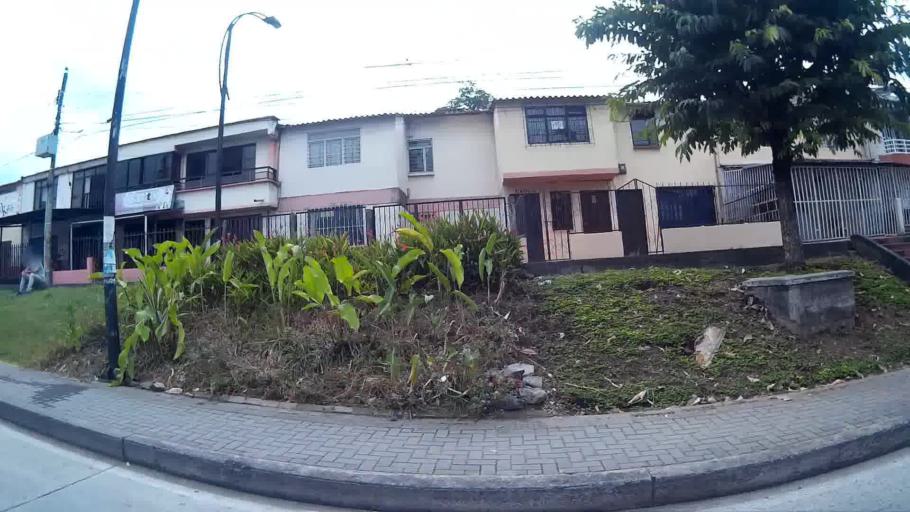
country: CO
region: Risaralda
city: Pereira
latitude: 4.8077
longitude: -75.7364
